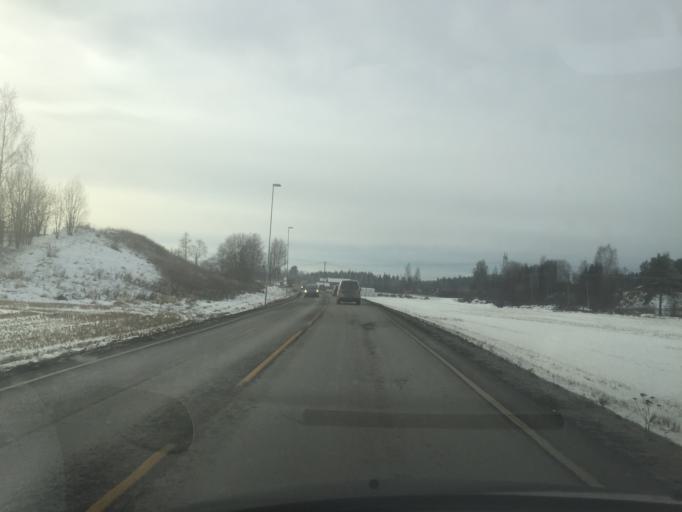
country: NO
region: Hedmark
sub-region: Loten
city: Loten
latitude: 60.8065
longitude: 11.2974
